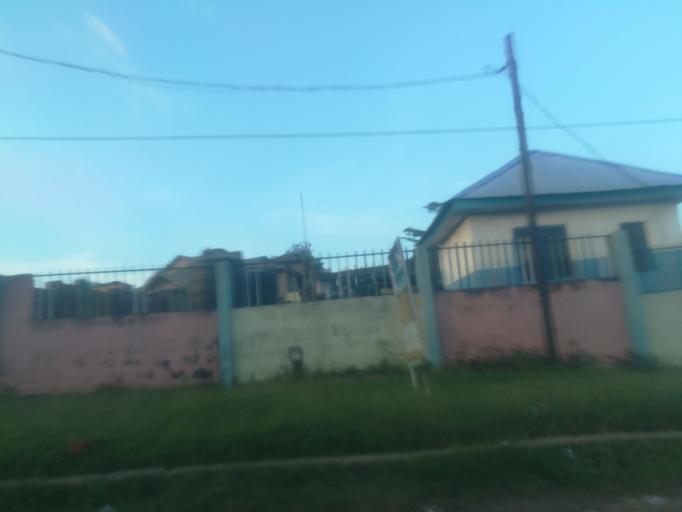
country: NG
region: Ogun
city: Abeokuta
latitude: 7.1487
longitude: 3.3347
